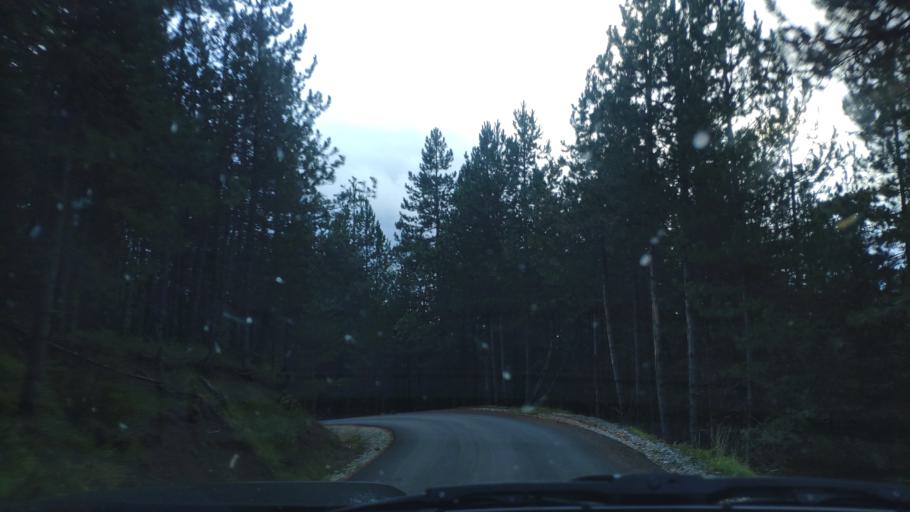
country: AL
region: Korce
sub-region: Rrethi i Kolonjes
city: Erseke
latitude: 40.2918
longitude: 20.8630
